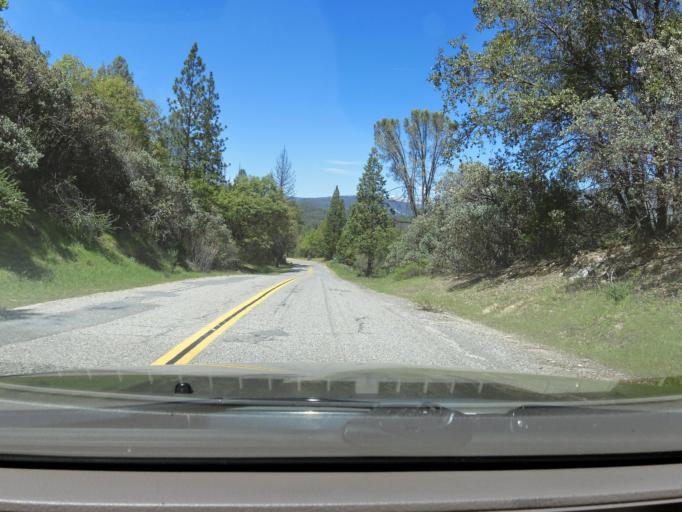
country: US
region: California
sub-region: Madera County
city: Oakhurst
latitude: 37.2429
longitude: -119.5184
